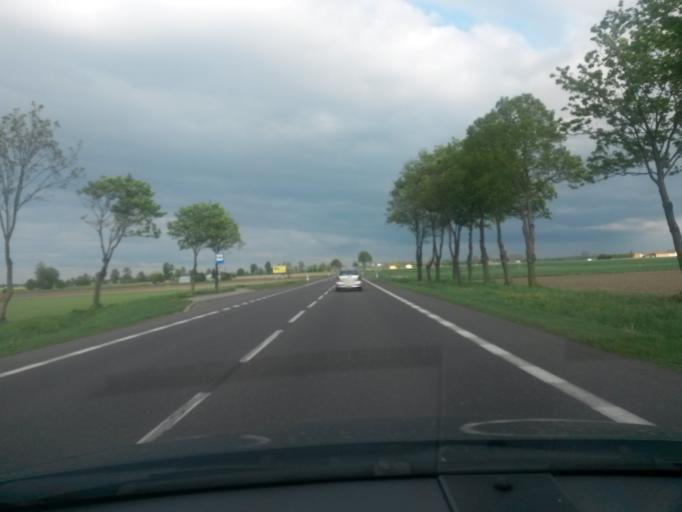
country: PL
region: Masovian Voivodeship
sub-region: Powiat plocki
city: Bulkowo
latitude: 52.6434
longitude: 20.1165
